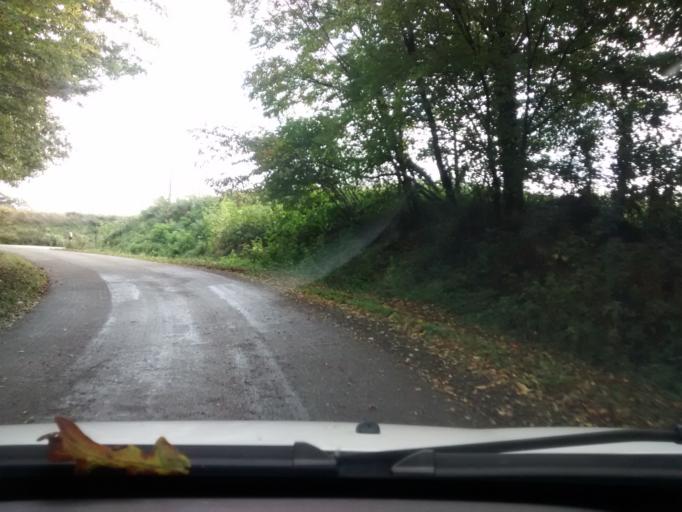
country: FR
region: Brittany
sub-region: Departement d'Ille-et-Vilaine
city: Chateaubourg
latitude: 48.1218
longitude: -1.3907
